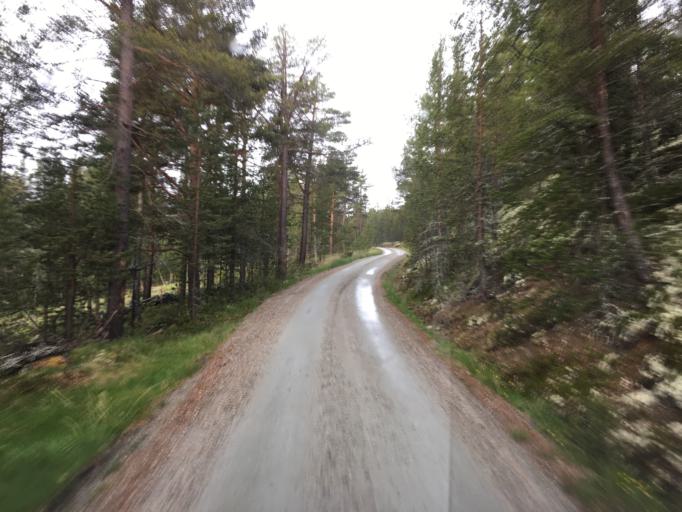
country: NO
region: Hedmark
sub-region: Folldal
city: Folldal
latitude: 62.0724
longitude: 9.9454
